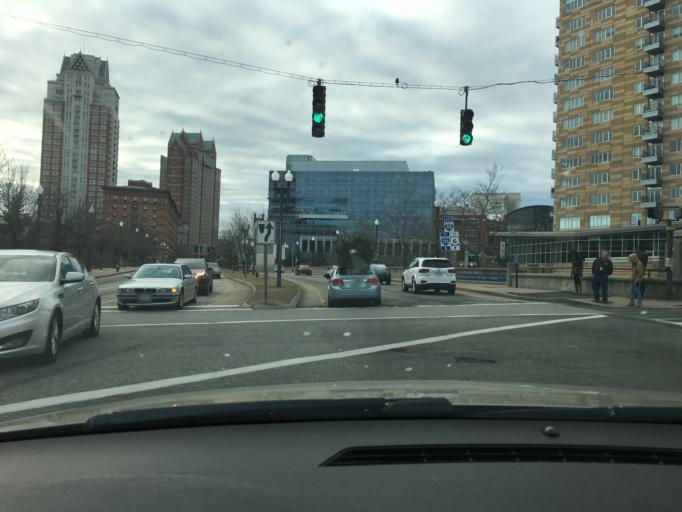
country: US
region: Rhode Island
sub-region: Providence County
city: Providence
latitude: 41.8269
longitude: -71.4121
